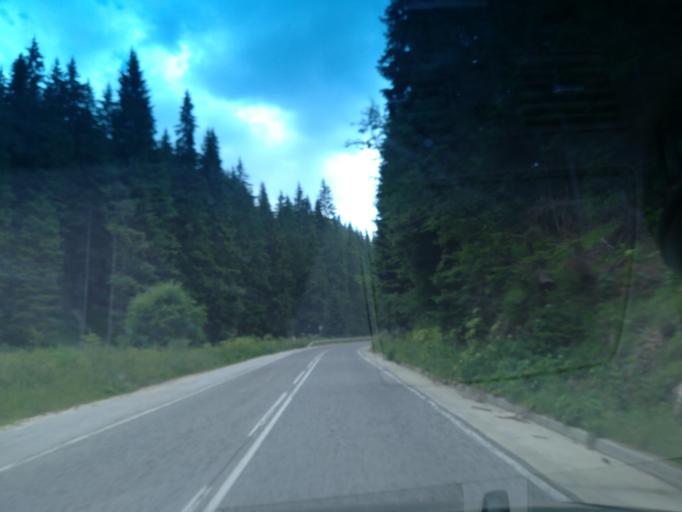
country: BG
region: Smolyan
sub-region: Obshtina Chepelare
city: Chepelare
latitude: 41.6658
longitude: 24.7144
